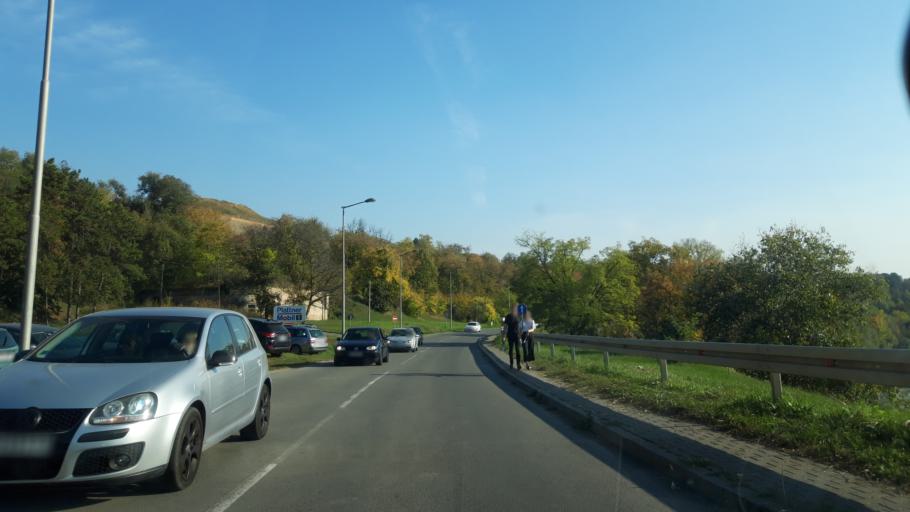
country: RS
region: Autonomna Pokrajina Vojvodina
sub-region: Juznobacki Okrug
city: Petrovaradin
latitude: 45.2492
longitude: 19.8641
